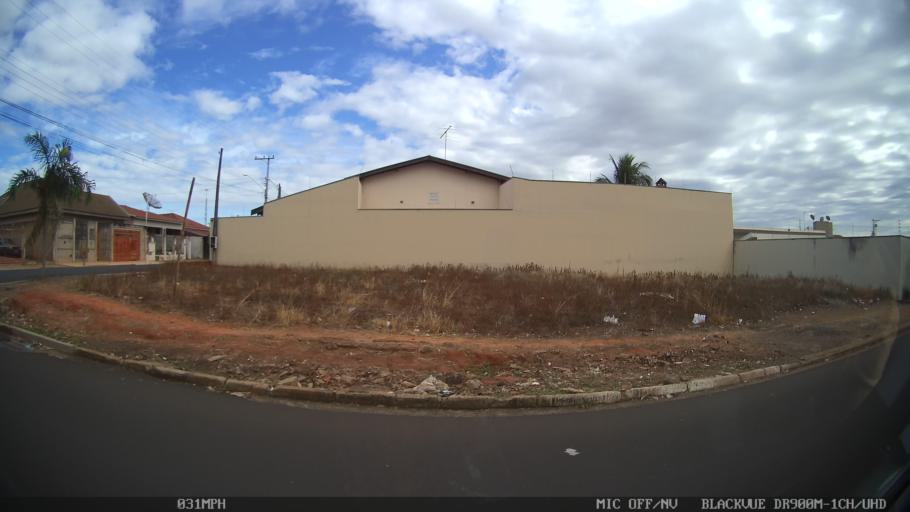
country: BR
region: Sao Paulo
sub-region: Sao Jose Do Rio Preto
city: Sao Jose do Rio Preto
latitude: -20.8119
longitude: -49.4970
